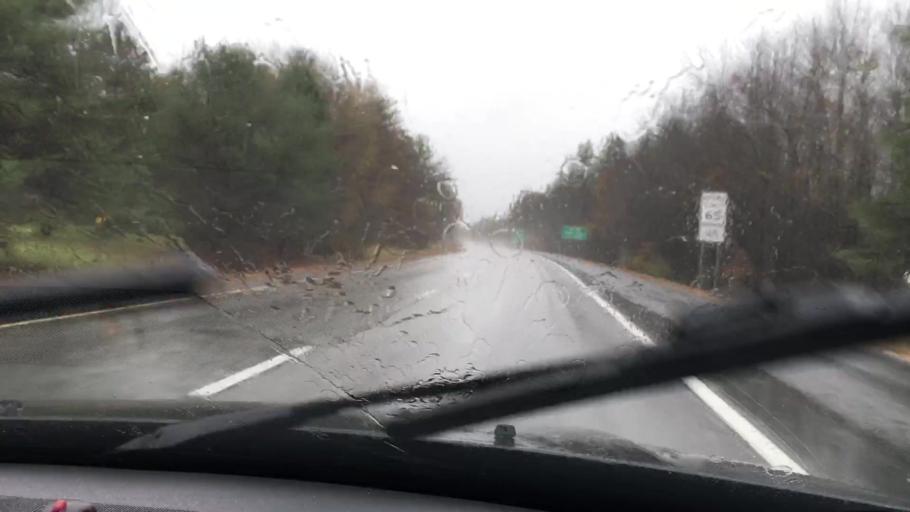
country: US
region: New Hampshire
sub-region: Merrimack County
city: Canterbury
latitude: 43.2981
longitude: -71.5792
